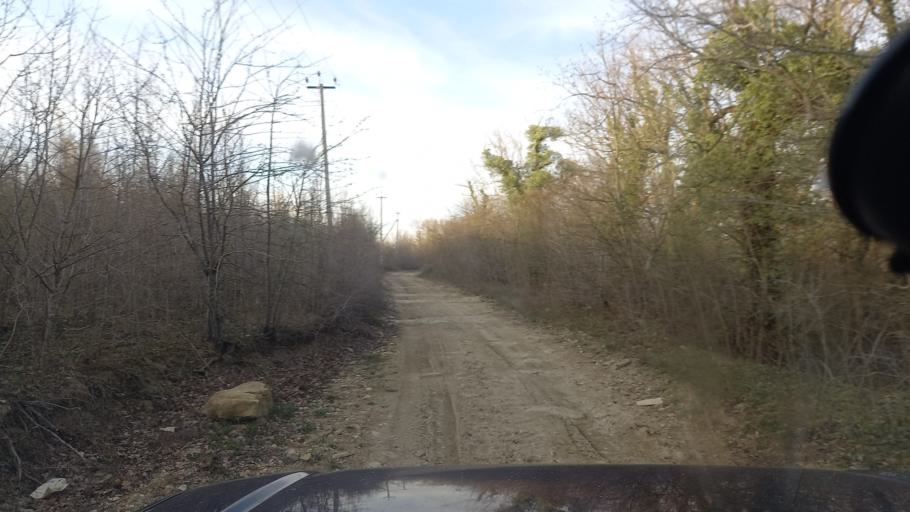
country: RU
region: Krasnodarskiy
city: Arkhipo-Osipovka
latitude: 44.3607
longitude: 38.5637
